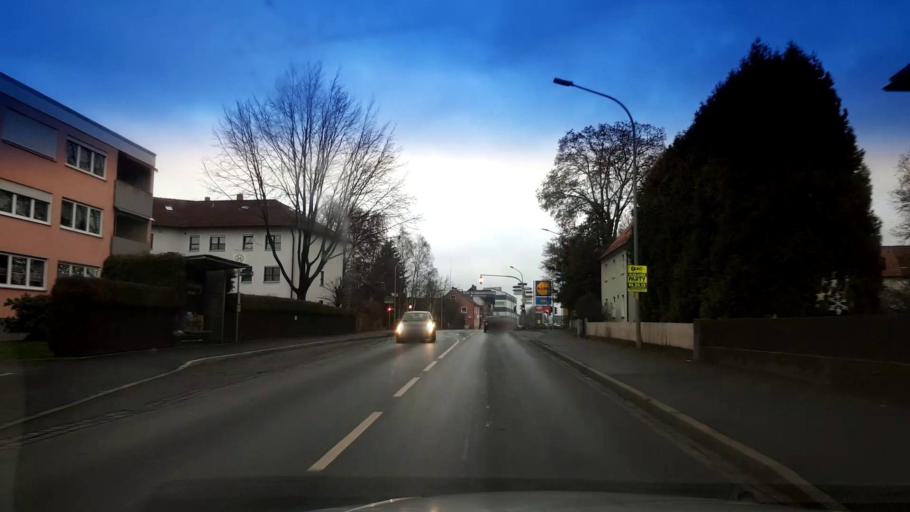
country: DE
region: Bavaria
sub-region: Upper Palatinate
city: Tirschenreuth
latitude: 49.8852
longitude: 12.3239
